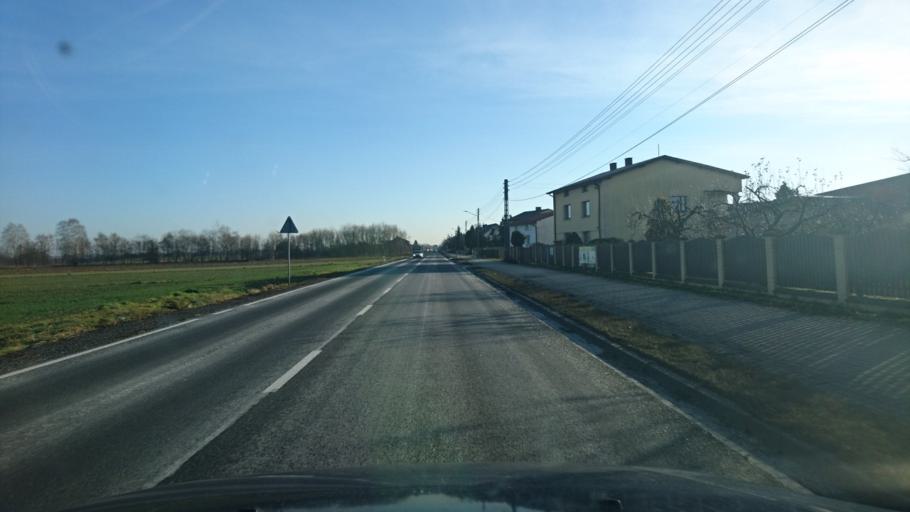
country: PL
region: Silesian Voivodeship
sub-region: Powiat klobucki
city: Starokrzepice
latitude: 51.0045
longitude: 18.6607
